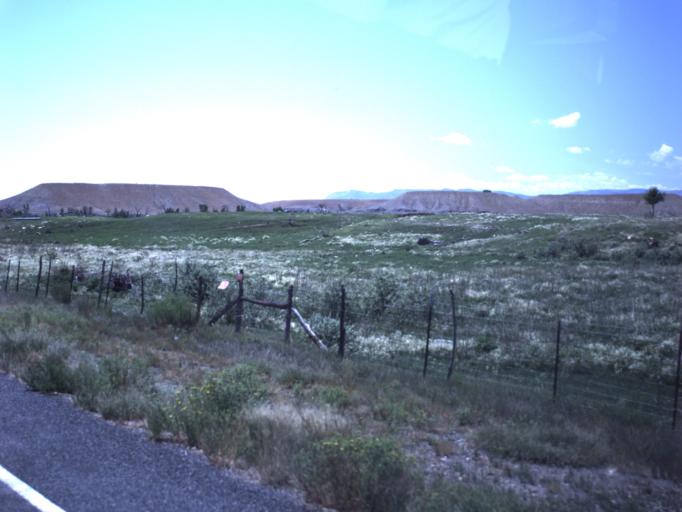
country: US
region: Utah
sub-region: Emery County
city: Castle Dale
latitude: 39.1913
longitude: -111.0477
